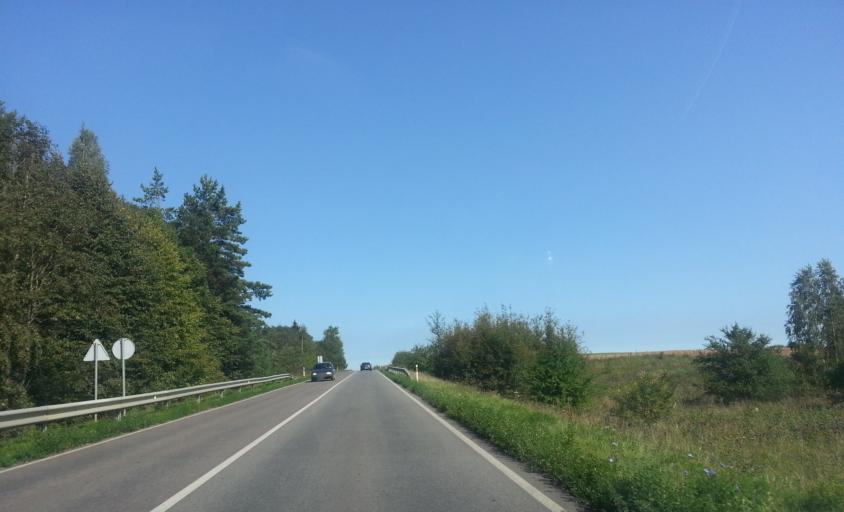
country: LT
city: Grigiskes
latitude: 54.7551
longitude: 25.0815
